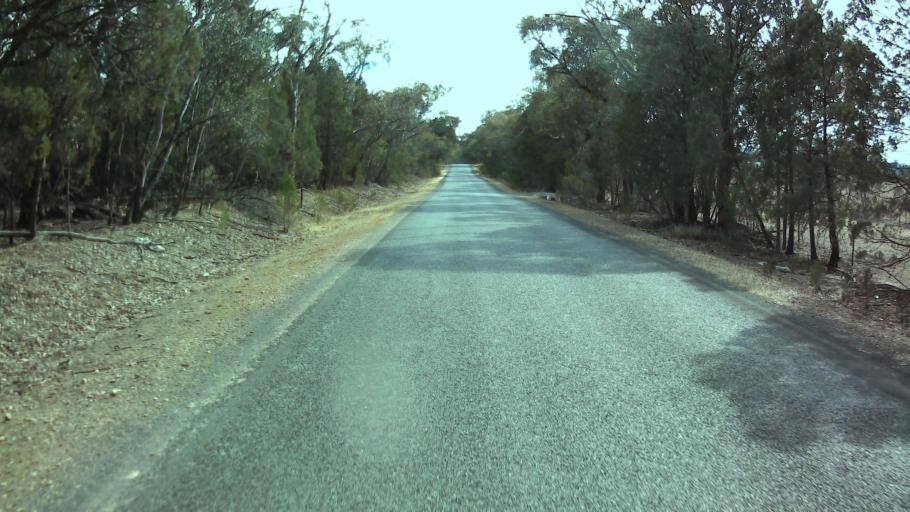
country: AU
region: New South Wales
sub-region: Weddin
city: Grenfell
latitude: -33.8931
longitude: 148.1895
